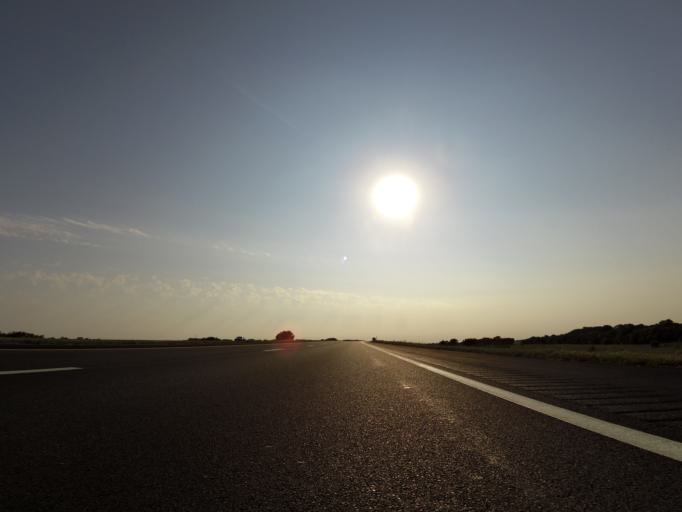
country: US
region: Kansas
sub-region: Reno County
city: Haven
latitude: 37.8751
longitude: -97.6865
